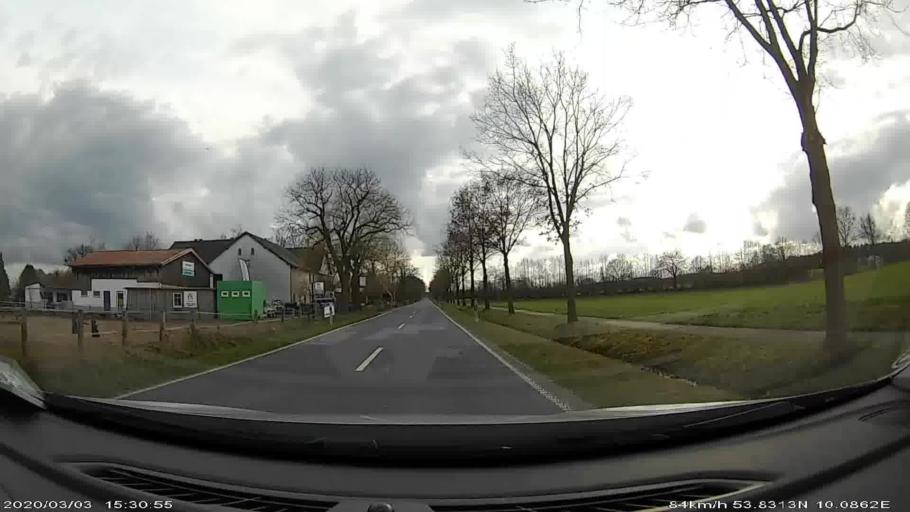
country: DE
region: Schleswig-Holstein
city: Huttblek
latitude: 53.8323
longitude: 10.0866
